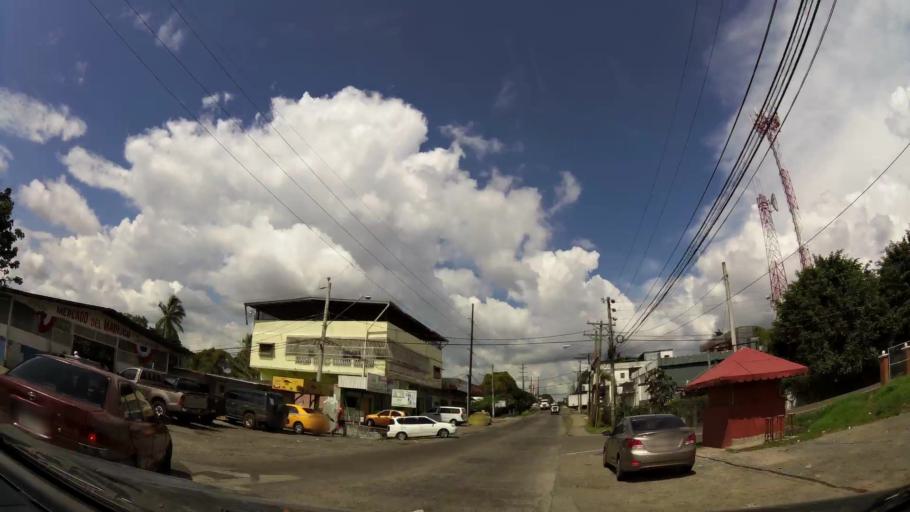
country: PA
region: Panama
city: Vista Alegre
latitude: 8.9250
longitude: -79.6992
